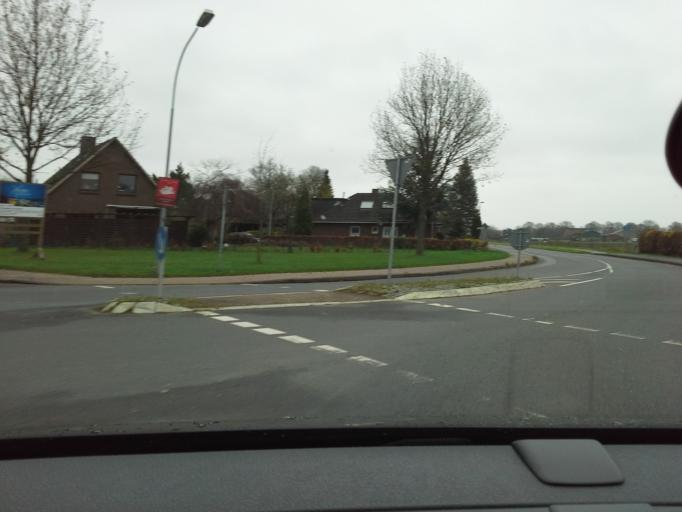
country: DE
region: Schleswig-Holstein
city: Hemdingen
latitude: 53.7662
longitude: 9.8466
